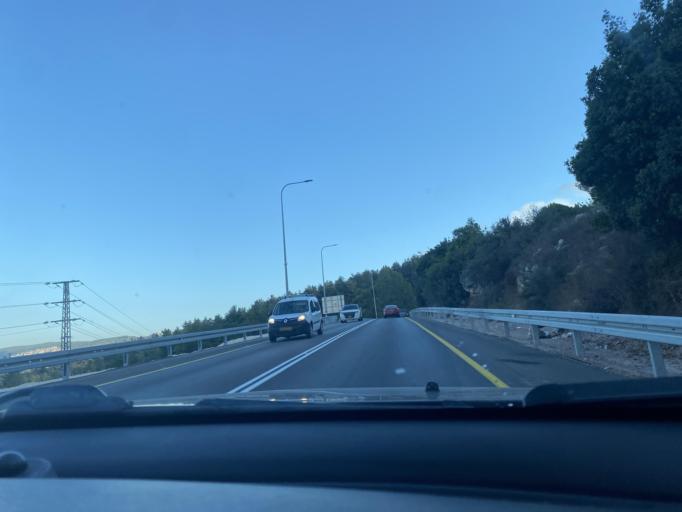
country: IL
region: Northern District
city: Kefar Weradim
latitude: 32.9999
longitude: 35.2820
